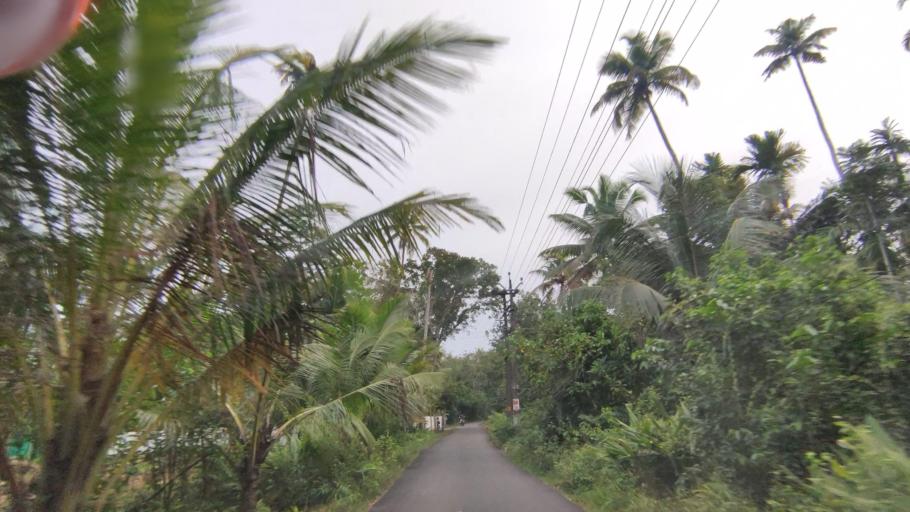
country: IN
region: Kerala
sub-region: Alappuzha
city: Shertallai
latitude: 9.6725
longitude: 76.3697
